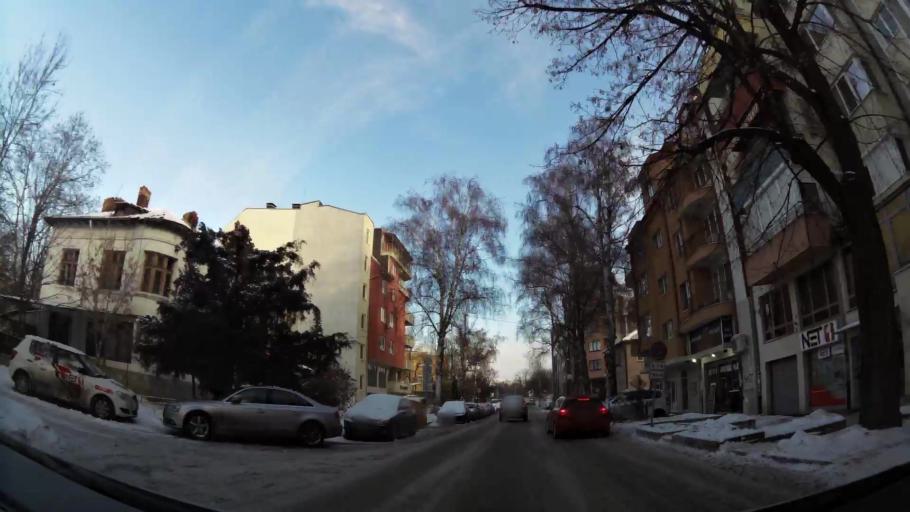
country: BG
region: Sofia-Capital
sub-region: Stolichna Obshtina
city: Sofia
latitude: 42.6731
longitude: 23.3336
